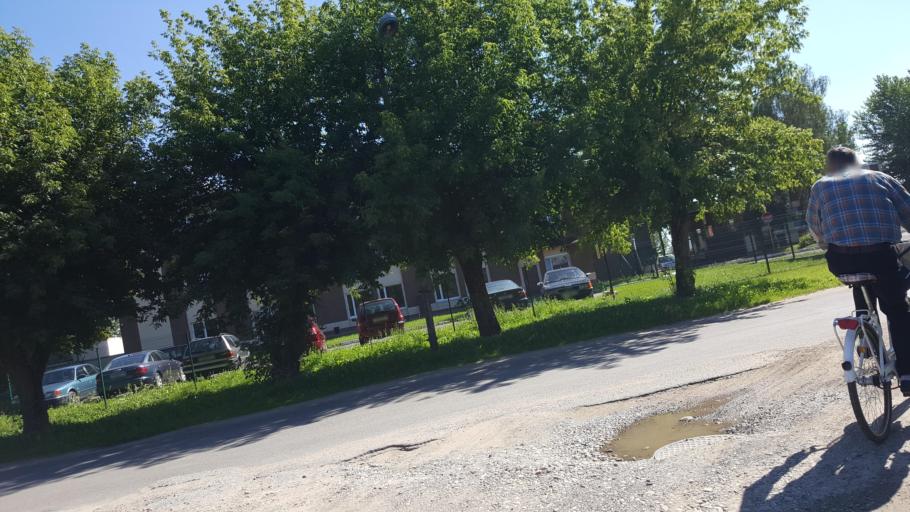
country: BY
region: Brest
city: Charnawchytsy
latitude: 52.2125
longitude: 23.7554
